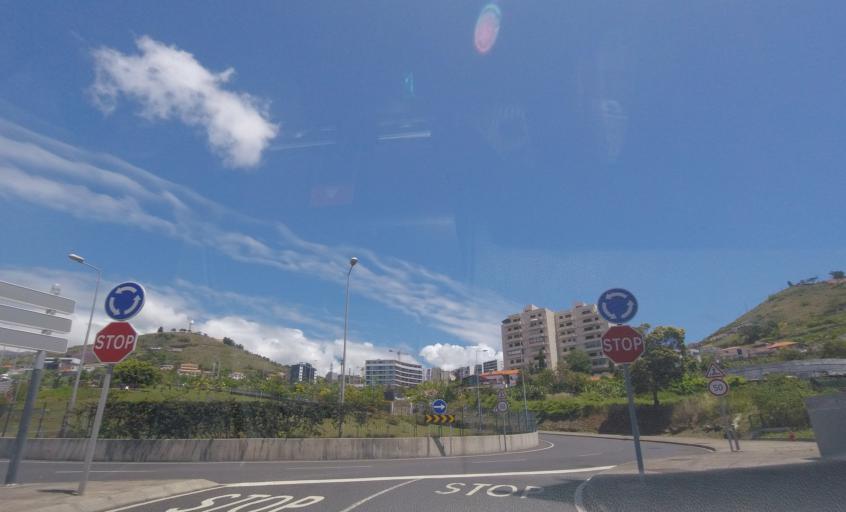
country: PT
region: Madeira
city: Camara de Lobos
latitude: 32.6428
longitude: -16.9461
